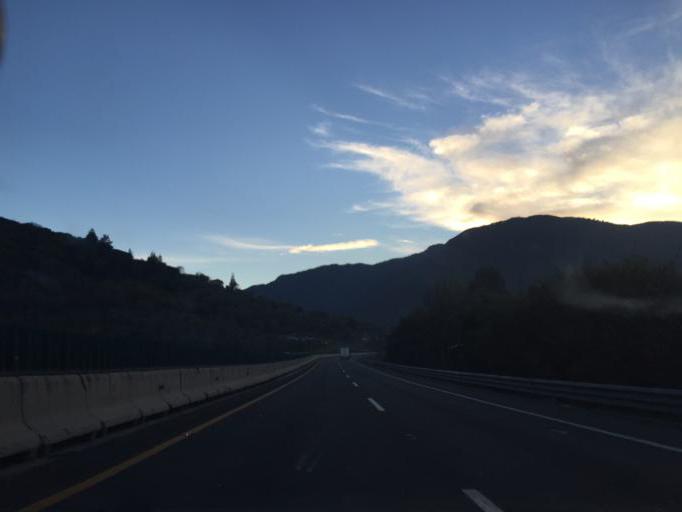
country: MX
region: Veracruz
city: Ciudad Mendoza
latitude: 18.8133
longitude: -97.1864
